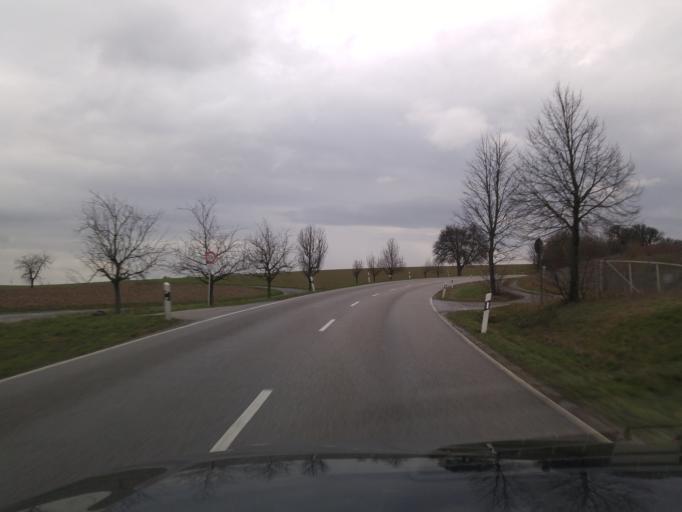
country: DE
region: Baden-Wuerttemberg
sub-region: Regierungsbezirk Stuttgart
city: Bretzfeld
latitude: 49.2132
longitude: 9.4619
